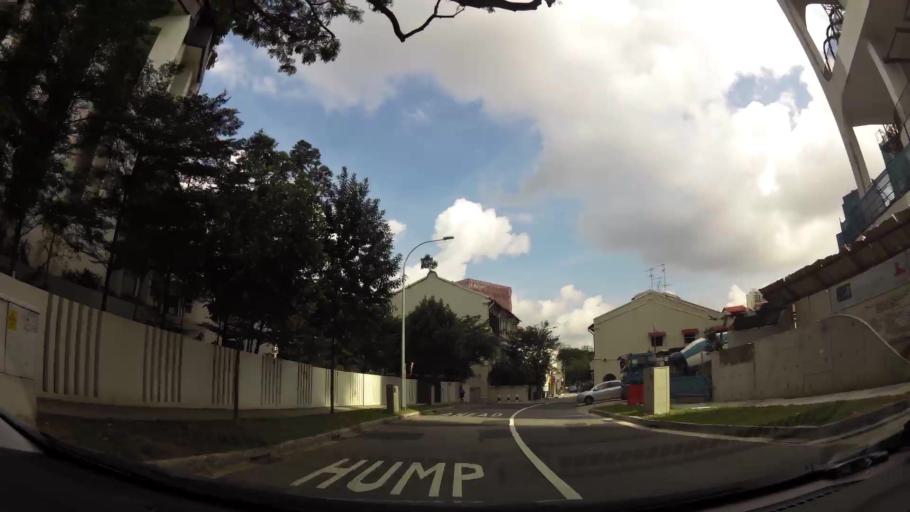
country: SG
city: Singapore
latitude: 1.2759
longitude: 103.8371
